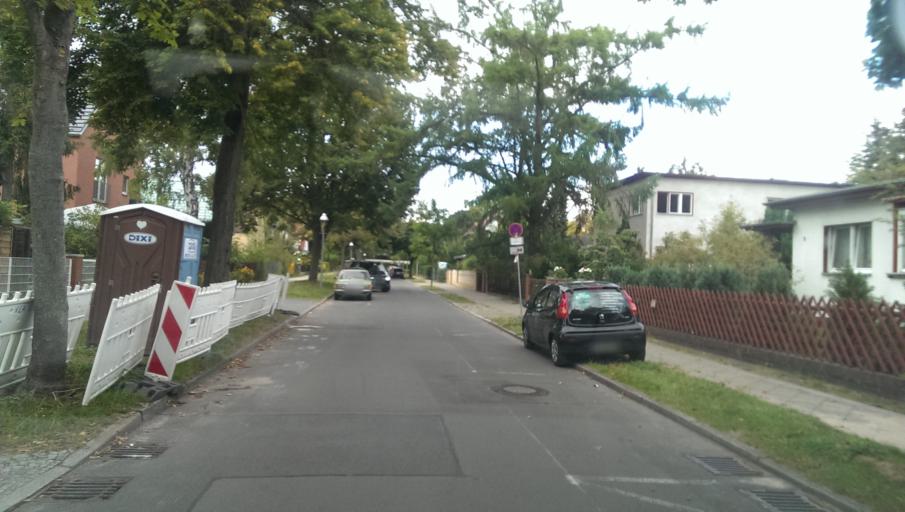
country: DE
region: Brandenburg
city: Teltow
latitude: 52.4151
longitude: 13.2623
